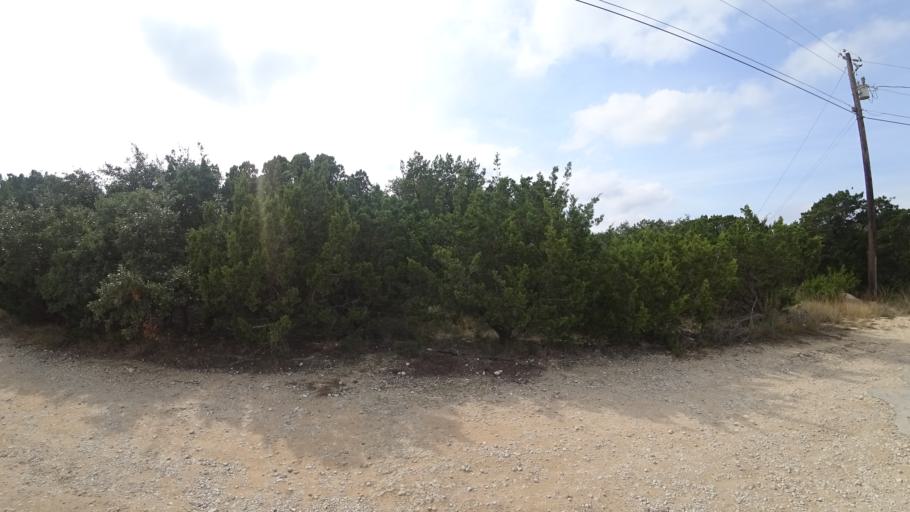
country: US
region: Texas
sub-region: Travis County
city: Hudson Bend
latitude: 30.3879
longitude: -97.9340
